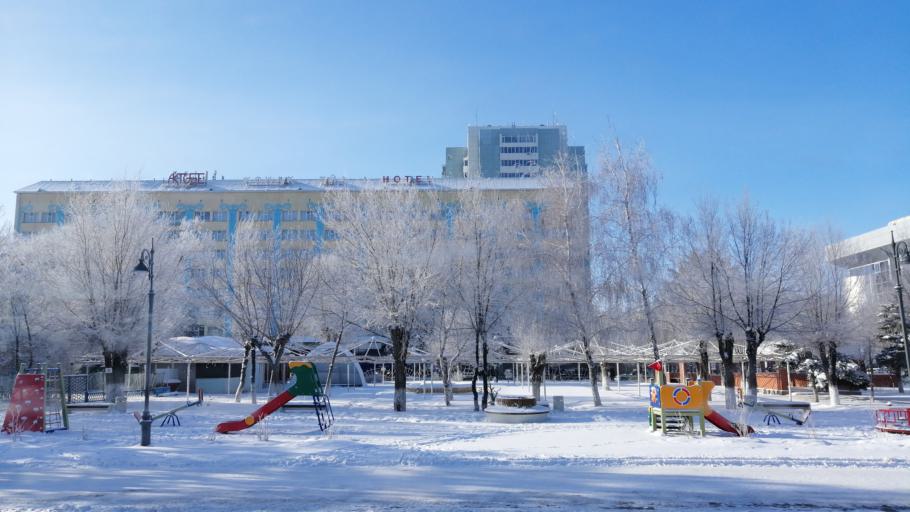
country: KZ
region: Aqtoebe
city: Aqtobe
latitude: 50.2985
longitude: 57.1558
